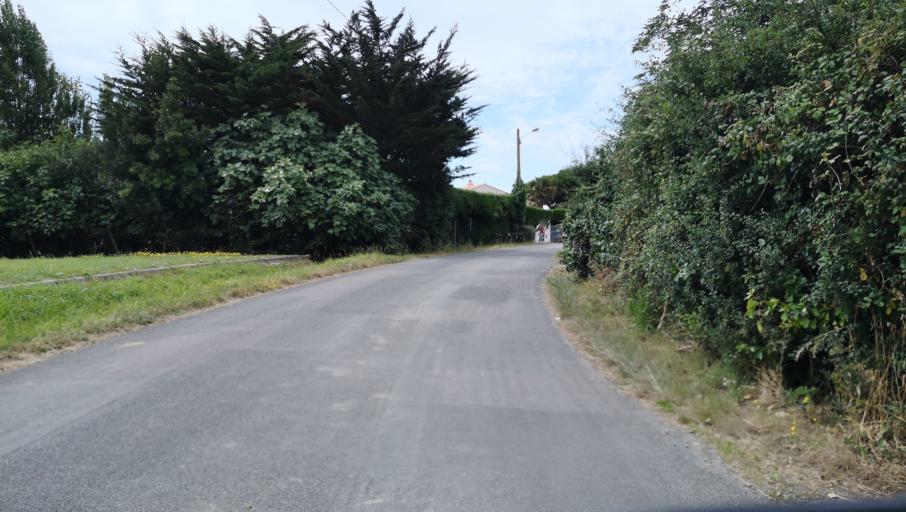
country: FR
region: Pays de la Loire
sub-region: Departement de la Vendee
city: Les Sables-d'Olonne
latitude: 46.5191
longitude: -1.7950
